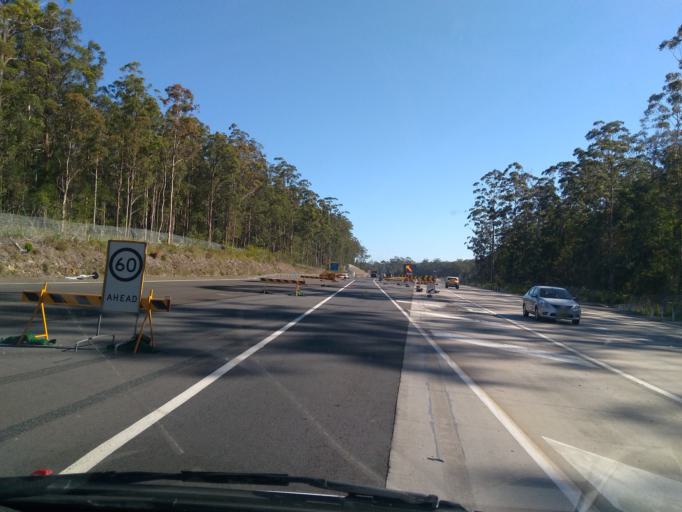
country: AU
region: New South Wales
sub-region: Kempsey
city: Crescent Head
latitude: -31.2538
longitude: 152.8187
